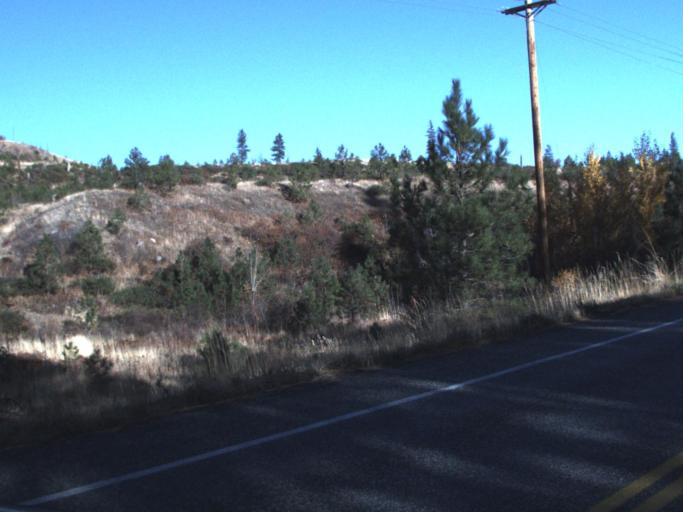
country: US
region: Washington
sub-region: Okanogan County
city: Coulee Dam
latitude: 48.0874
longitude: -118.6930
